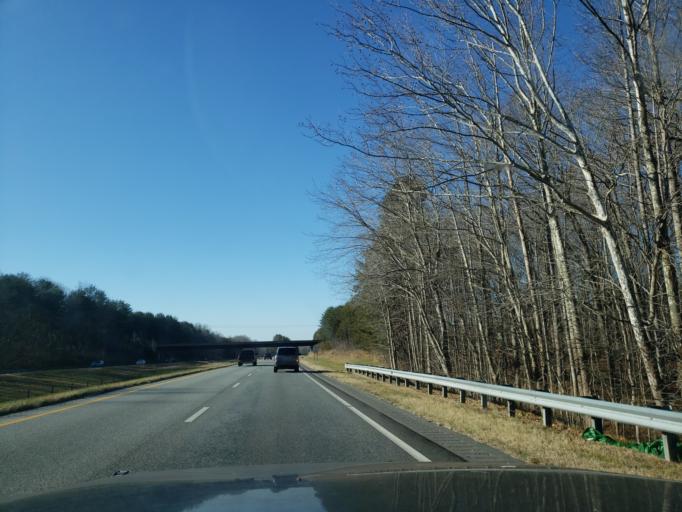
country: US
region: North Carolina
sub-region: Davidson County
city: Wallburg
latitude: 36.0303
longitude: -80.0704
